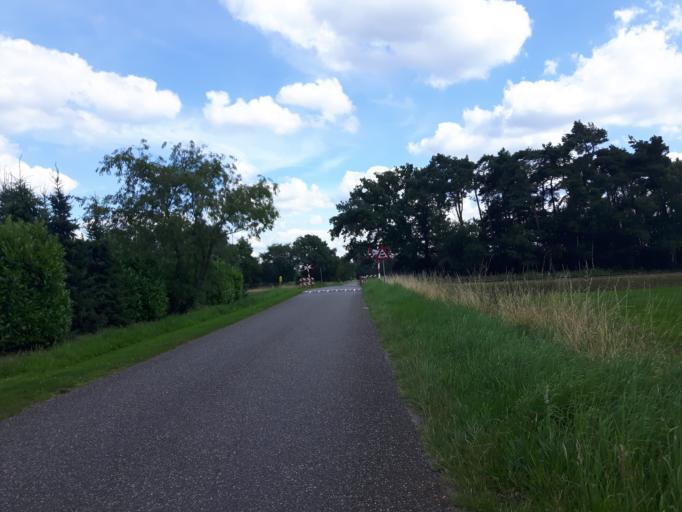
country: NL
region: Overijssel
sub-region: Gemeente Haaksbergen
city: Haaksbergen
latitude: 52.1869
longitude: 6.7784
